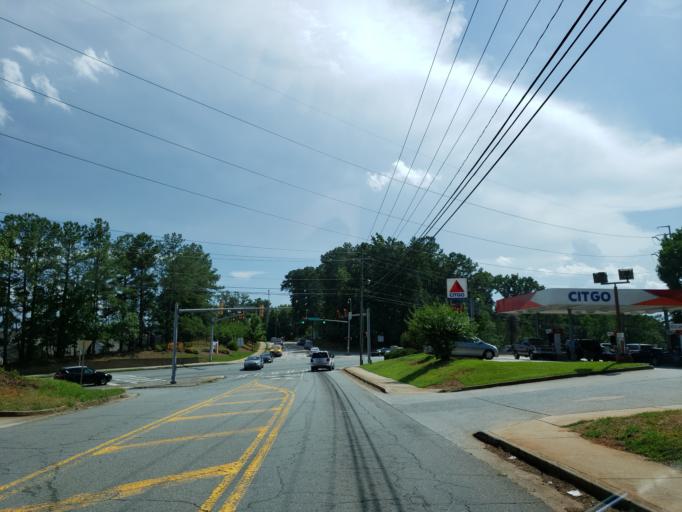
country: US
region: Georgia
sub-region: Cobb County
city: Fair Oaks
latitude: 33.8951
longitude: -84.5435
